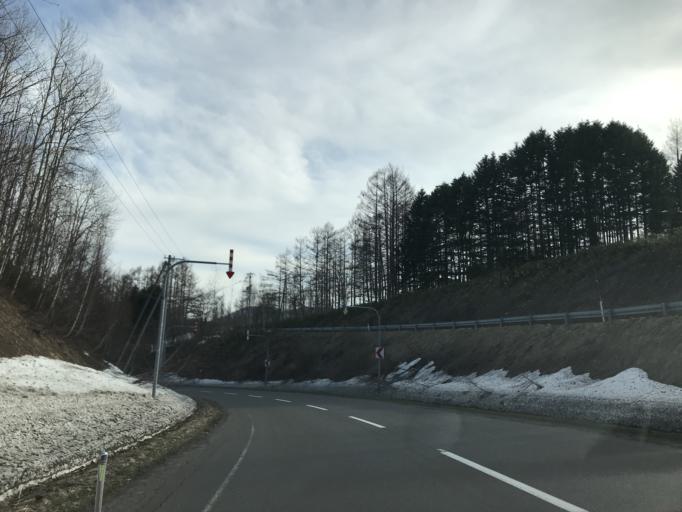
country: JP
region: Hokkaido
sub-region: Asahikawa-shi
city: Asahikawa
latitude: 43.6997
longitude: 142.3240
